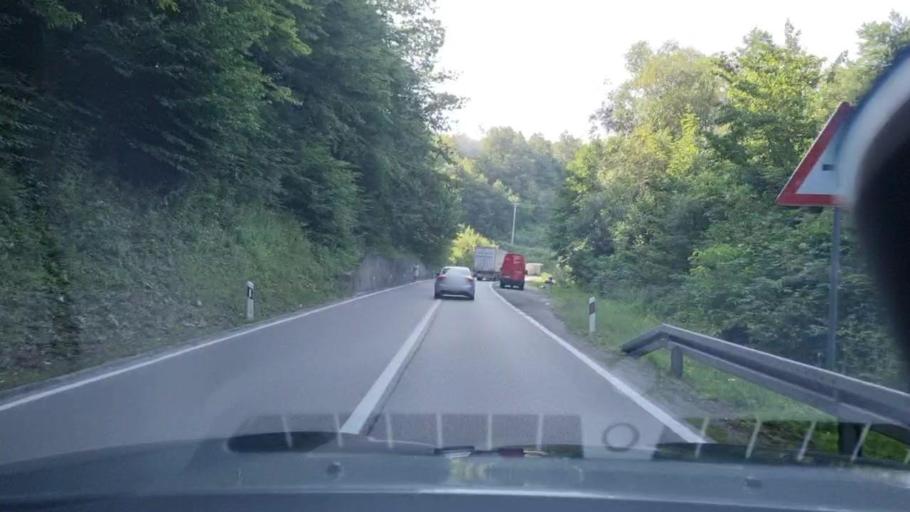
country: BA
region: Federation of Bosnia and Herzegovina
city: Skokovi
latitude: 45.0107
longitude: 15.9040
